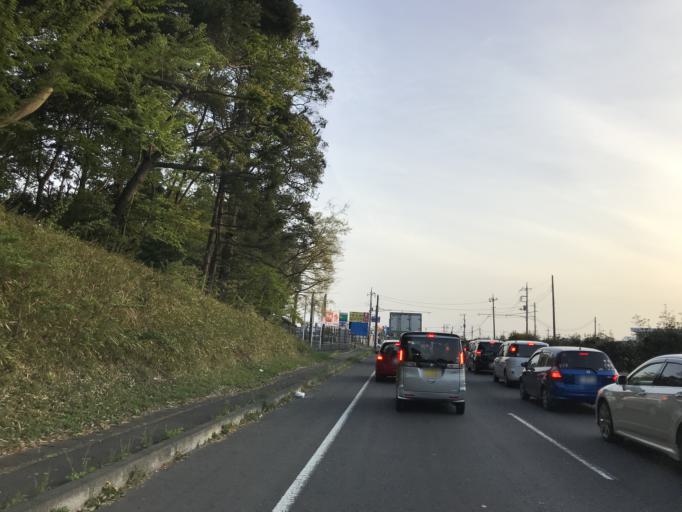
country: JP
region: Ibaraki
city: Mito-shi
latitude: 36.3510
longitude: 140.4939
